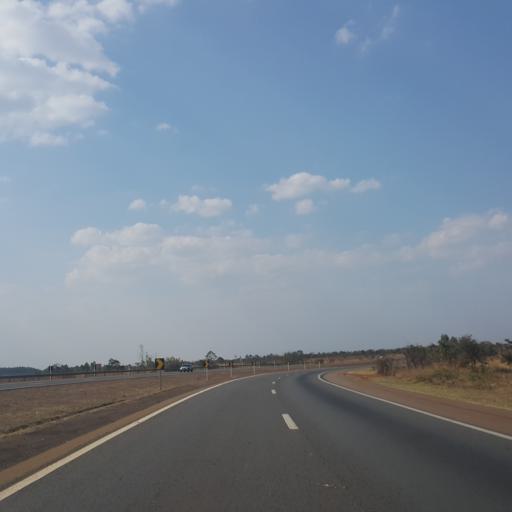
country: BR
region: Goias
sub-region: Abadiania
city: Abadiania
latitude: -16.2038
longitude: -48.7397
